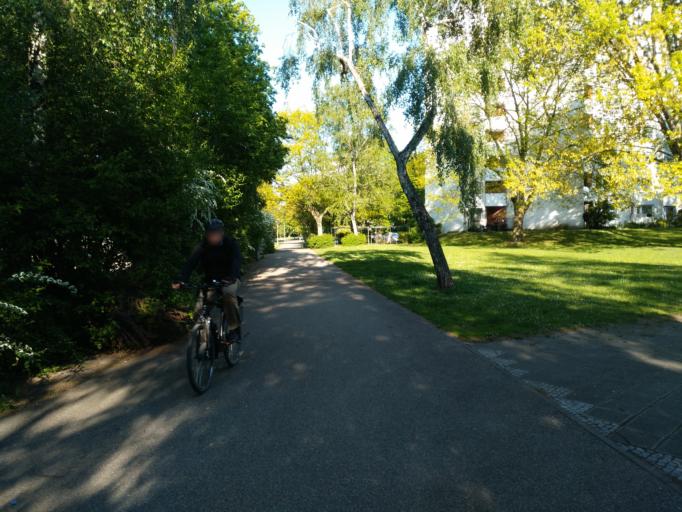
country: DE
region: Bavaria
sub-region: Regierungsbezirk Mittelfranken
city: Grossreuth bei Schweinau
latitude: 49.4446
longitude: 11.0383
